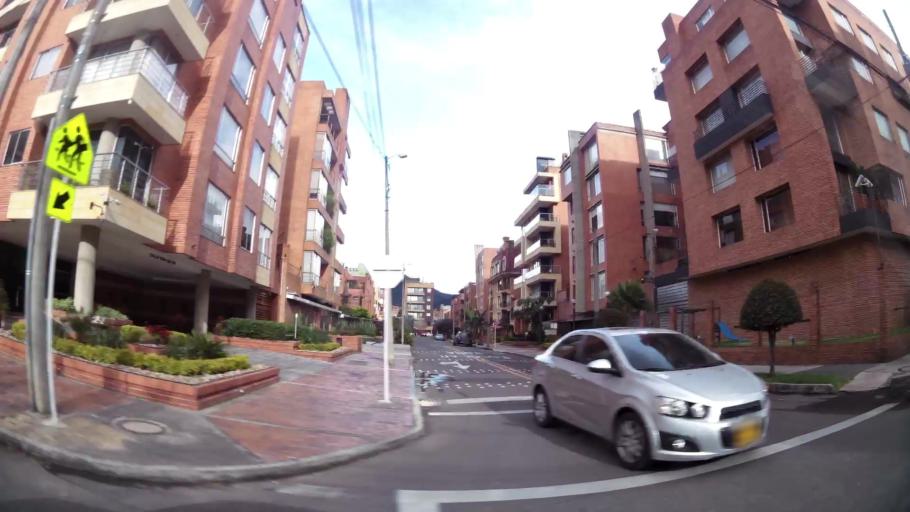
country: CO
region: Bogota D.C.
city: Barrio San Luis
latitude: 4.6900
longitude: -74.0538
